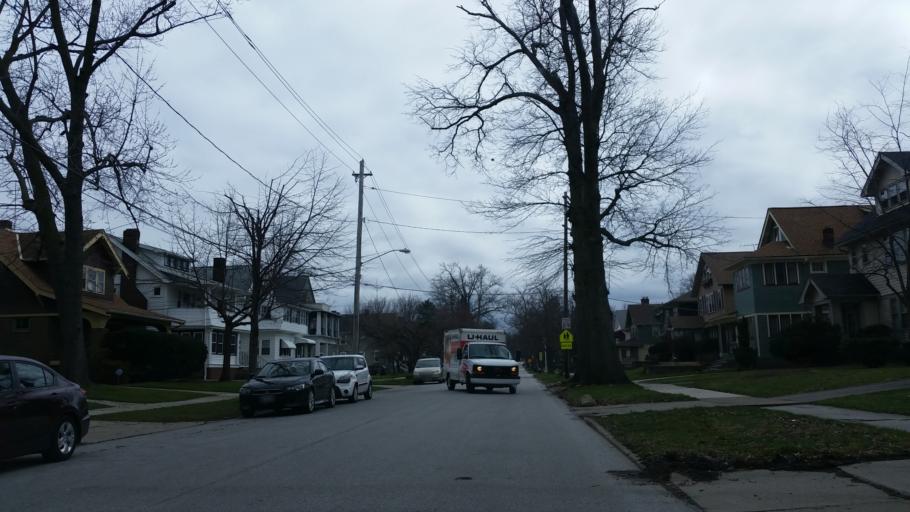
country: US
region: Ohio
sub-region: Cuyahoga County
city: Lakewood
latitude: 41.4902
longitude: -81.7828
